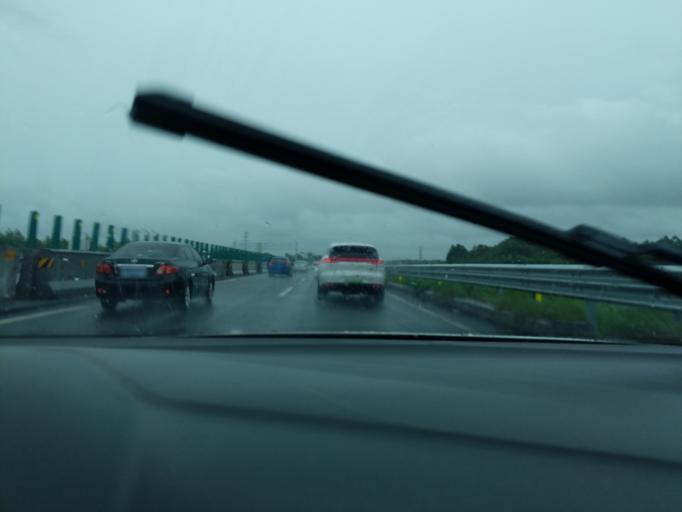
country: CN
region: Guangdong
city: Yueshan
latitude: 22.4625
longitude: 112.6918
